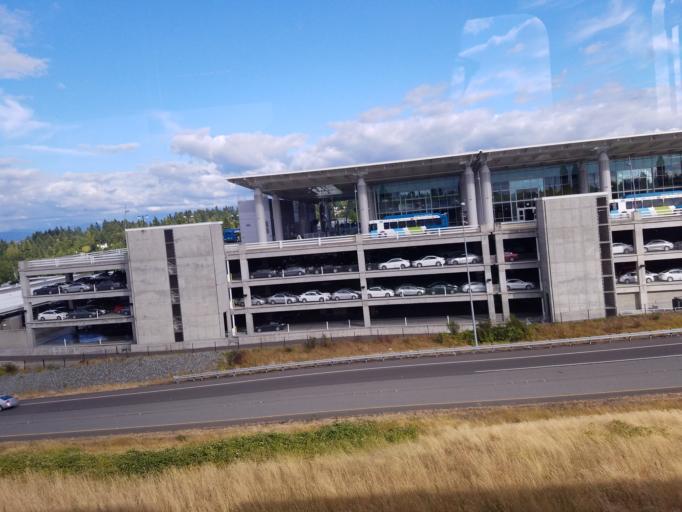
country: US
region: Washington
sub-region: King County
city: SeaTac
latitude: 47.4594
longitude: -122.2975
